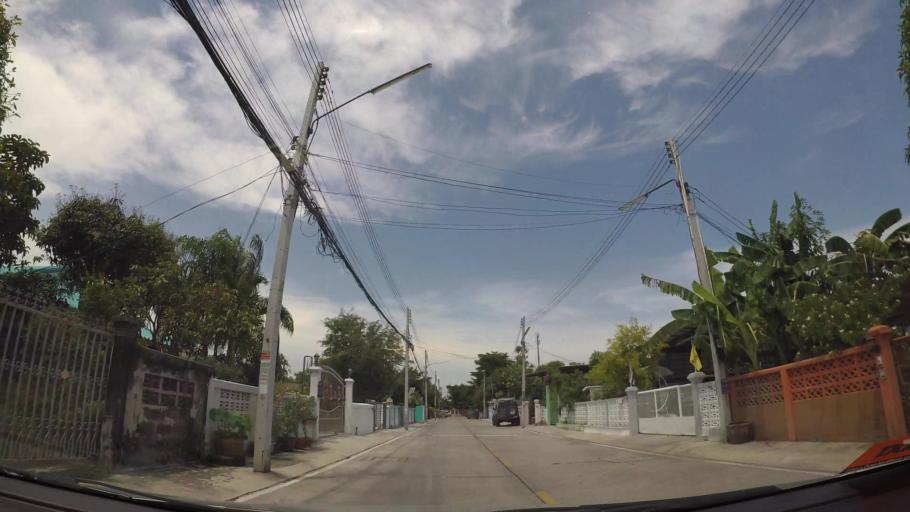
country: TH
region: Chon Buri
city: Chon Buri
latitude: 13.3318
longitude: 100.9474
